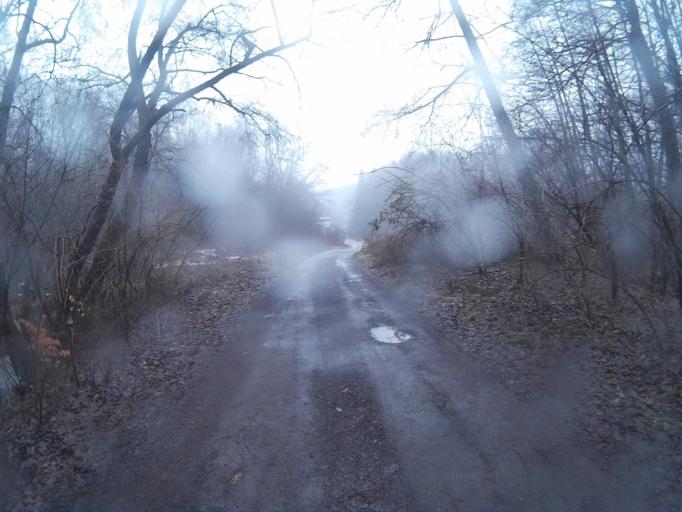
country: HU
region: Nograd
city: Somoskoujfalu
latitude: 48.1580
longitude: 19.8530
